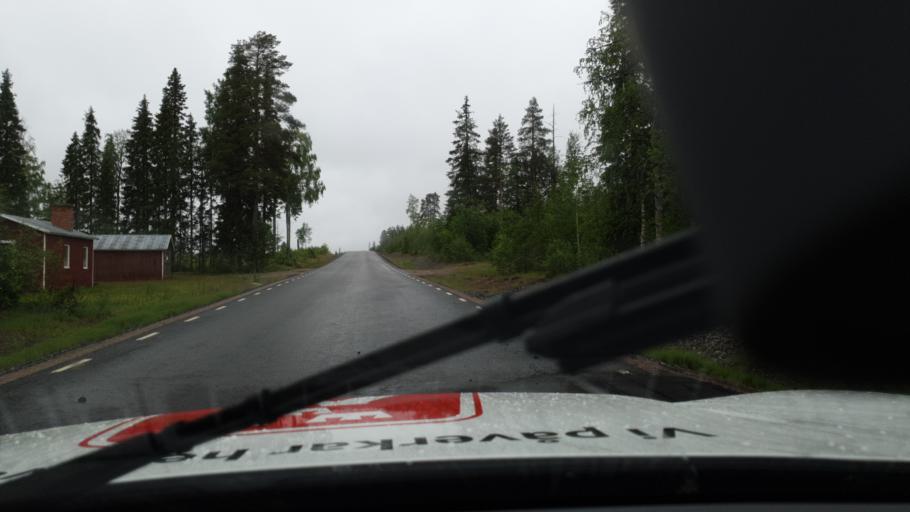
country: SE
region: Norrbotten
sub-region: Overtornea Kommun
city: OEvertornea
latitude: 66.5790
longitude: 23.3303
